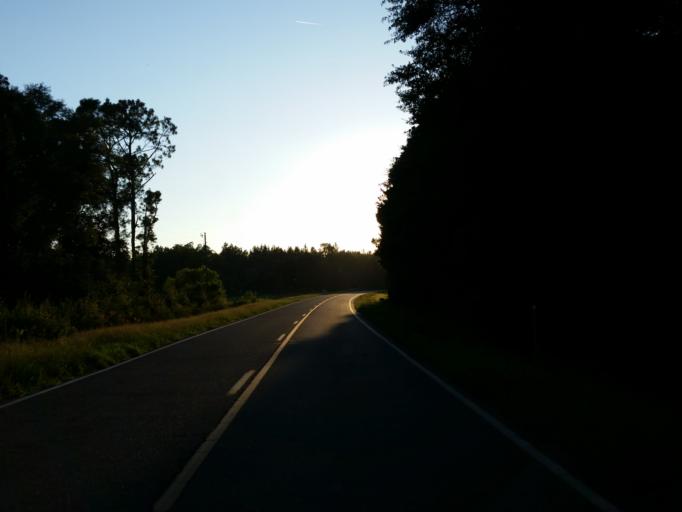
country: US
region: Georgia
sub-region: Berrien County
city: Nashville
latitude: 31.1796
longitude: -83.1353
